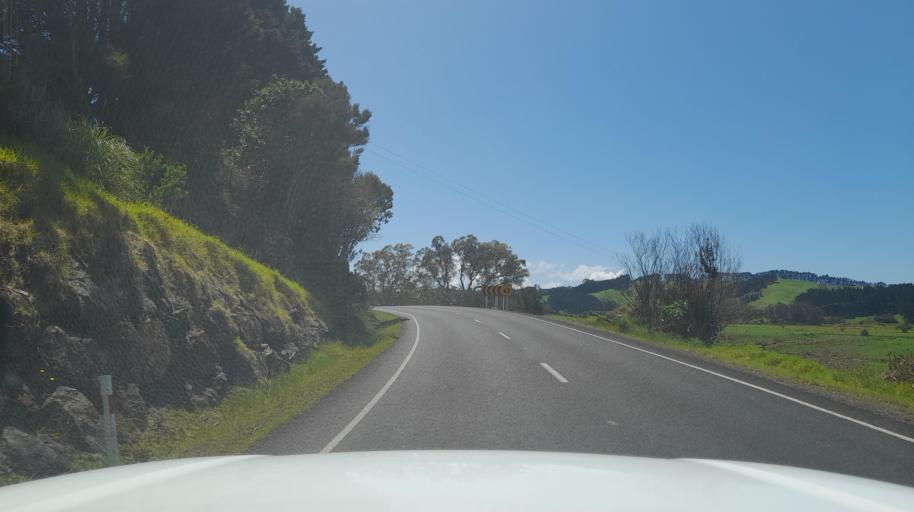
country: NZ
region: Northland
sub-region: Far North District
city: Taipa
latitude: -35.0318
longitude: 173.4855
